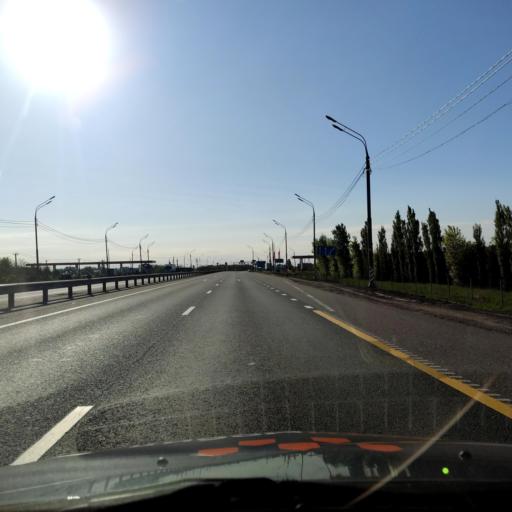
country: RU
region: Lipetsk
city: Khlevnoye
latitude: 52.2196
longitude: 39.1288
